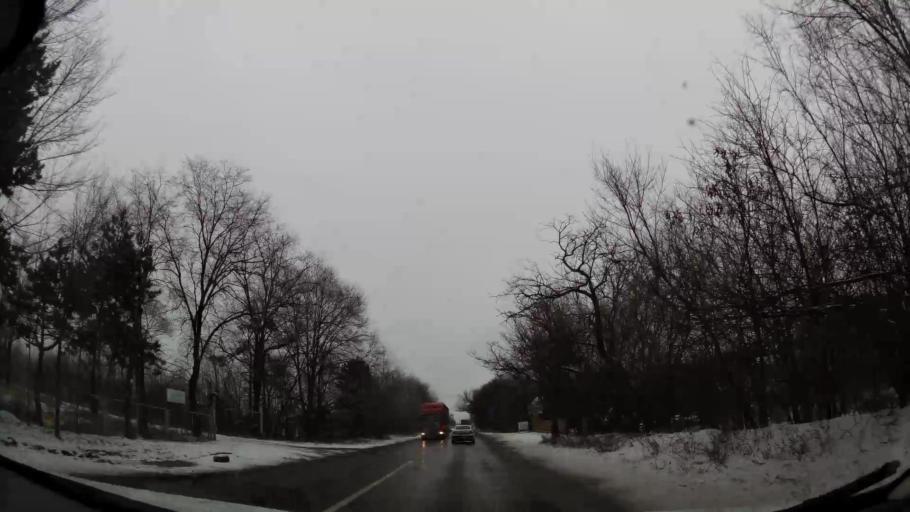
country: RO
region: Dambovita
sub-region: Comuna Ulmi
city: Ulmi
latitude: 44.8971
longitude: 25.5070
